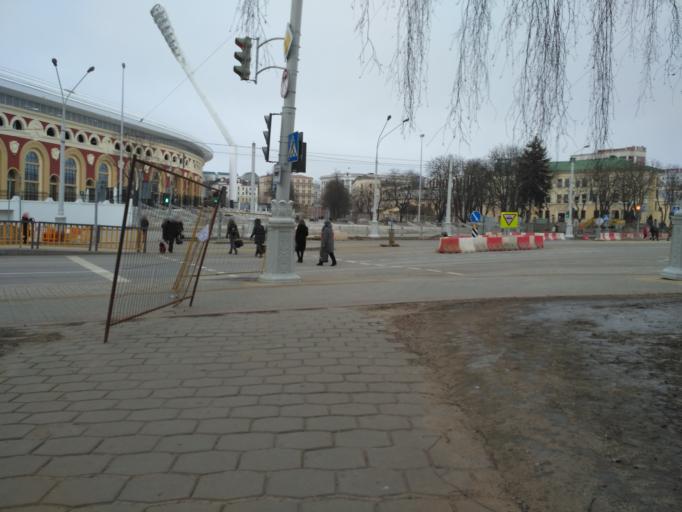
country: BY
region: Minsk
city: Minsk
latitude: 53.8941
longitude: 27.5624
